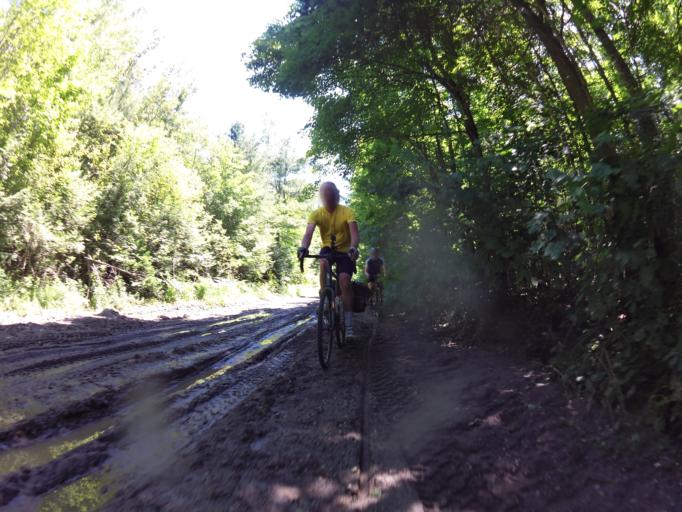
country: CA
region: Ontario
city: Perth
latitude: 45.0234
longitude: -76.6303
